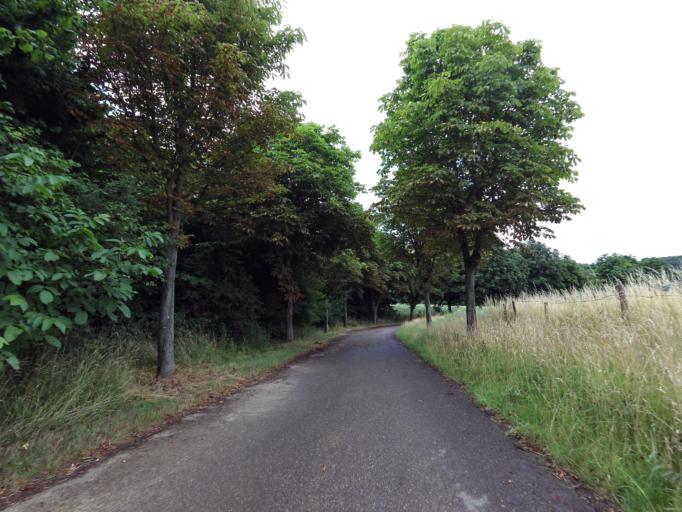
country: NL
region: Limburg
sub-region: Gemeente Kerkrade
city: Kerkrade
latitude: 50.8791
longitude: 6.0441
